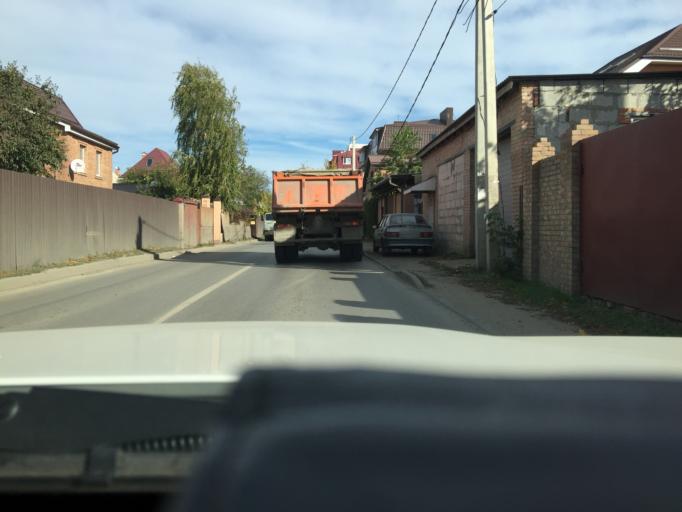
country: RU
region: Rostov
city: Imeni Chkalova
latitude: 47.2801
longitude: 39.7993
